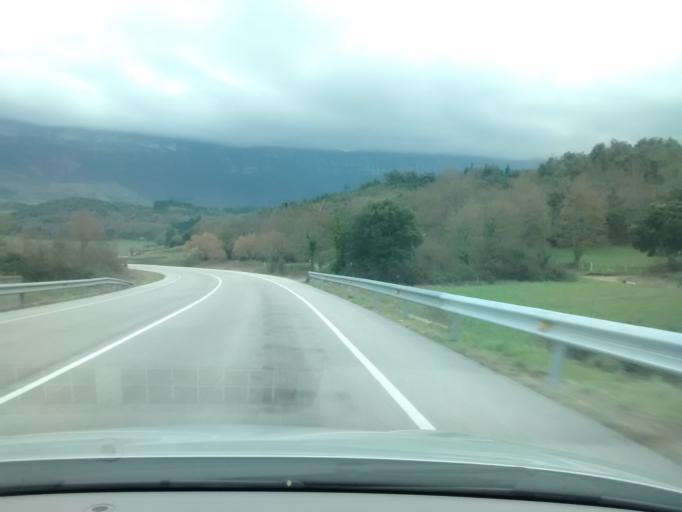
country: ES
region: Castille and Leon
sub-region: Provincia de Burgos
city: Villasana de Mena
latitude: 43.0986
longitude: -3.3066
